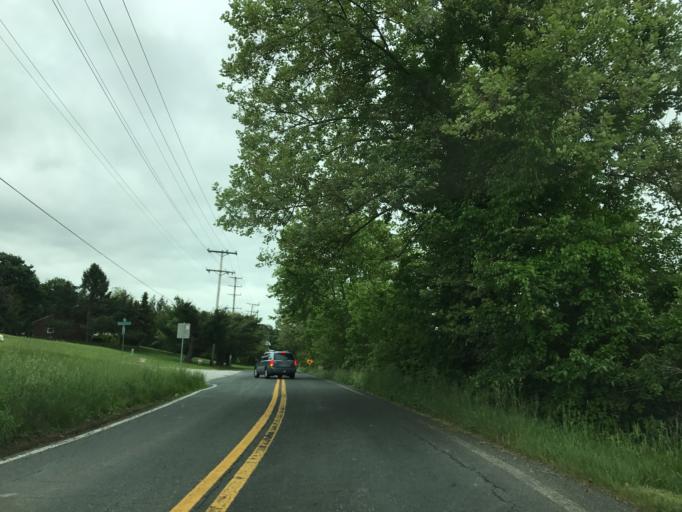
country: US
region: Maryland
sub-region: Carroll County
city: Hampstead
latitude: 39.6116
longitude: -76.8793
